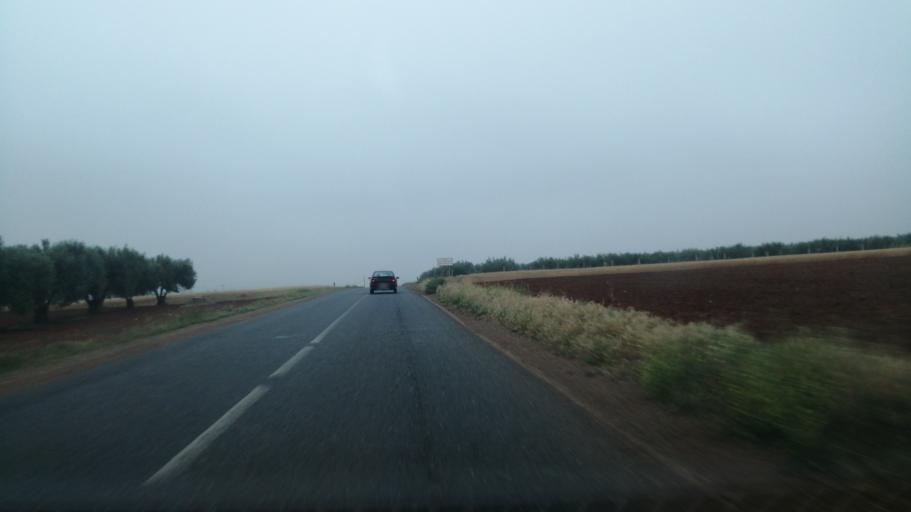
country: MA
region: Rabat-Sale-Zemmour-Zaer
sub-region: Khemisset
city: Tiflet
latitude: 33.7470
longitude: -6.2681
